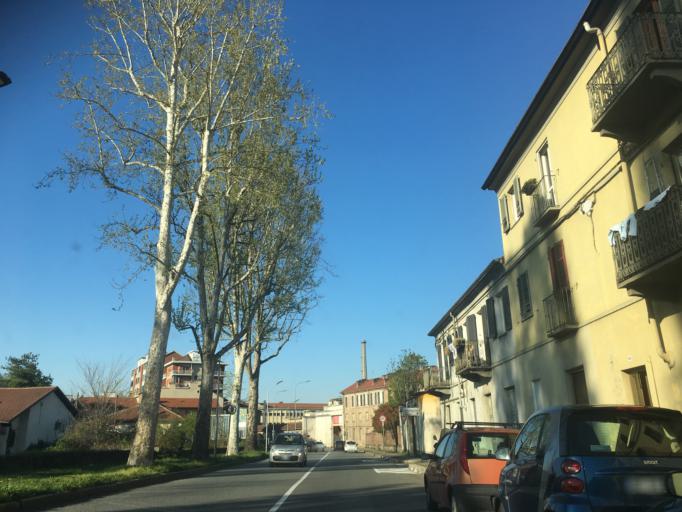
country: IT
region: Piedmont
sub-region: Provincia di Torino
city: Turin
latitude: 45.0876
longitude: 7.7140
